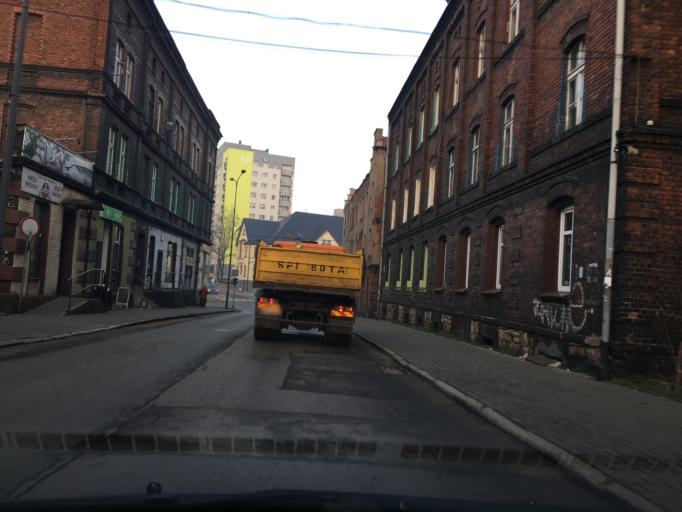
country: PL
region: Silesian Voivodeship
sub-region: Bytom
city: Bytom
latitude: 50.3372
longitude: 18.8908
